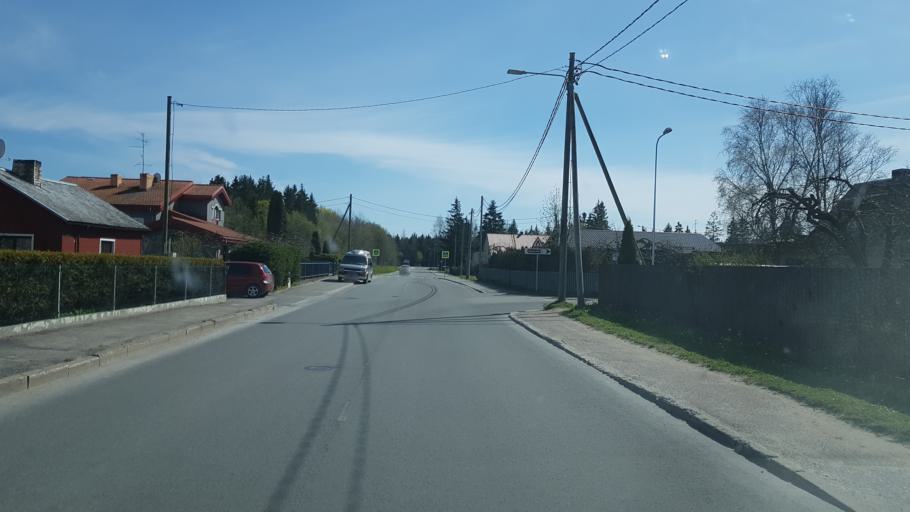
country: EE
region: Harju
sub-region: Keila linn
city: Keila
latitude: 59.3017
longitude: 24.4256
